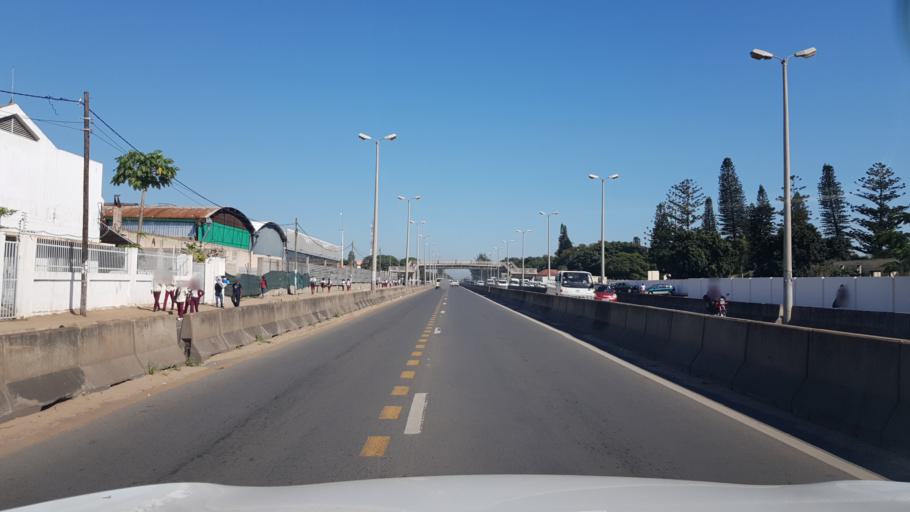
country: MZ
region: Maputo City
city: Maputo
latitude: -25.9381
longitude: 32.5471
